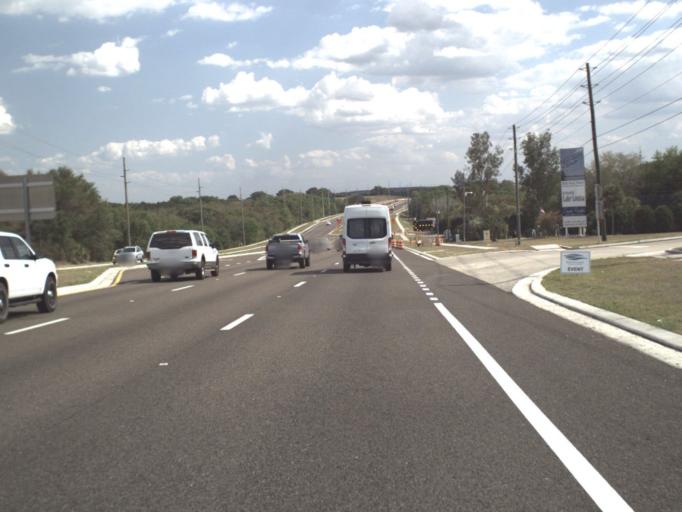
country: US
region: Florida
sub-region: Lake County
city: Clermont
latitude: 28.4984
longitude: -81.7185
